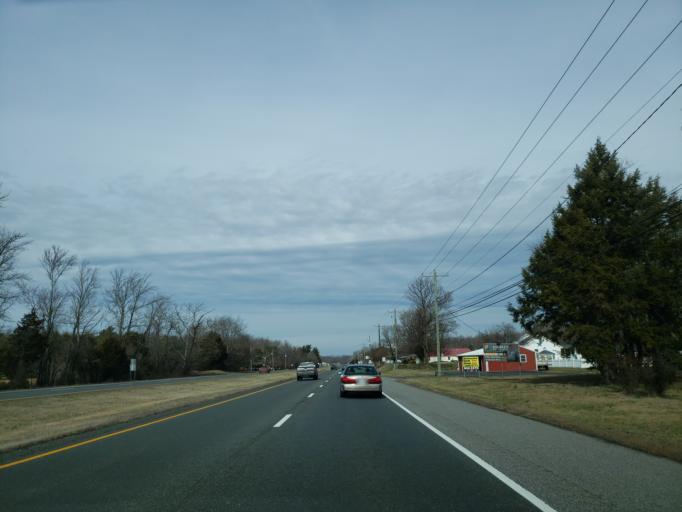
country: US
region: Delaware
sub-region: Kent County
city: Smyrna
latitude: 39.3383
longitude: -75.6317
